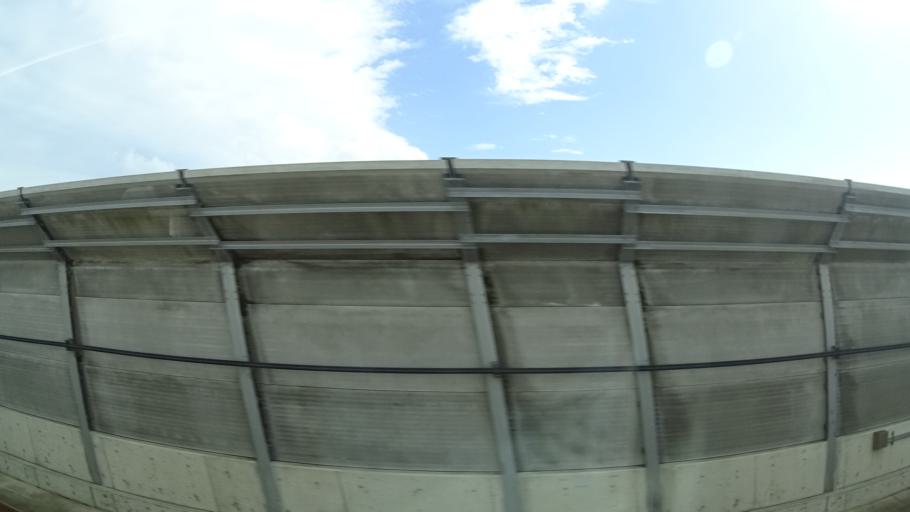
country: JP
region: Toyama
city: Takaoka
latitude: 36.7238
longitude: 137.0354
